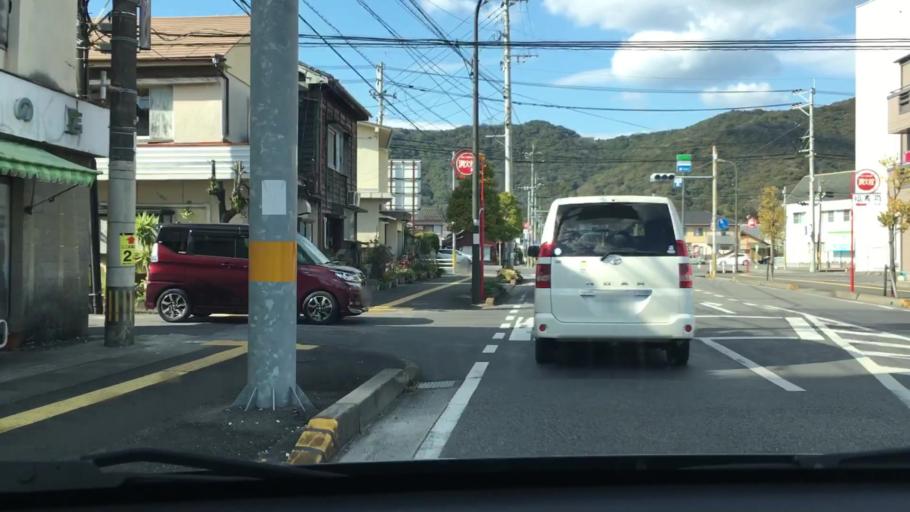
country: JP
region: Oita
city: Saiki
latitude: 32.9613
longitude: 131.9000
